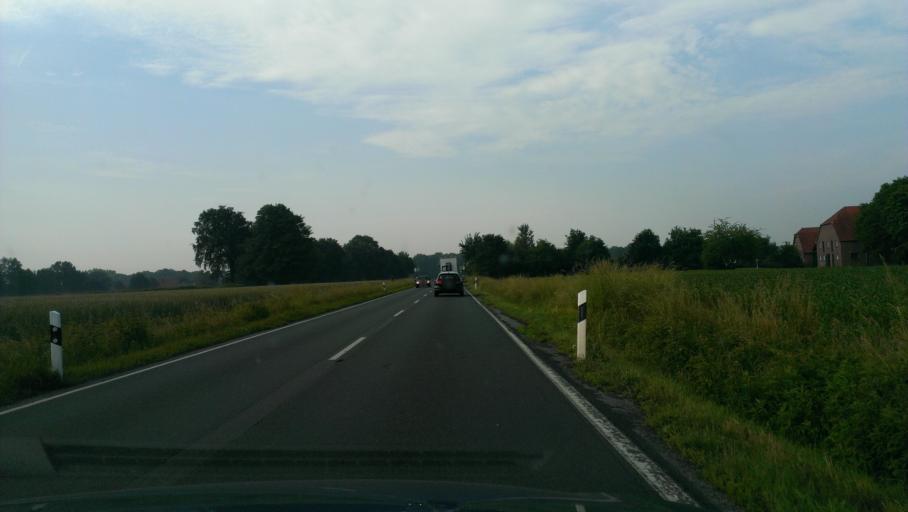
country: DE
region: North Rhine-Westphalia
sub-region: Regierungsbezirk Munster
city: Muenster
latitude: 51.8979
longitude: 7.6982
